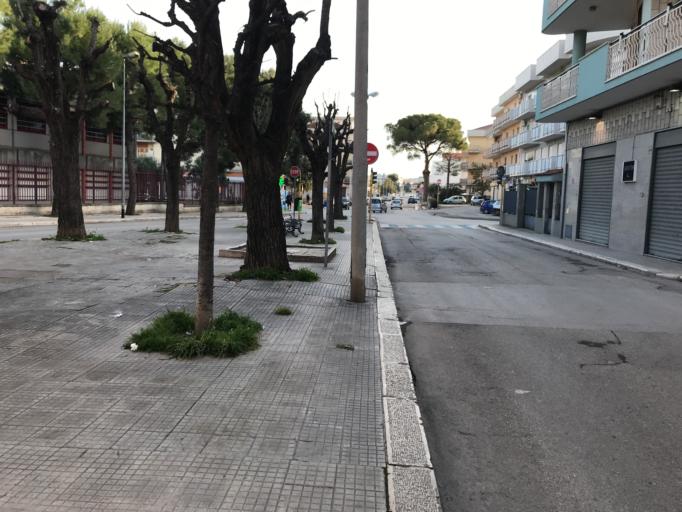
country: IT
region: Apulia
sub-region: Provincia di Bari
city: Corato
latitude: 41.1477
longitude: 16.4097
